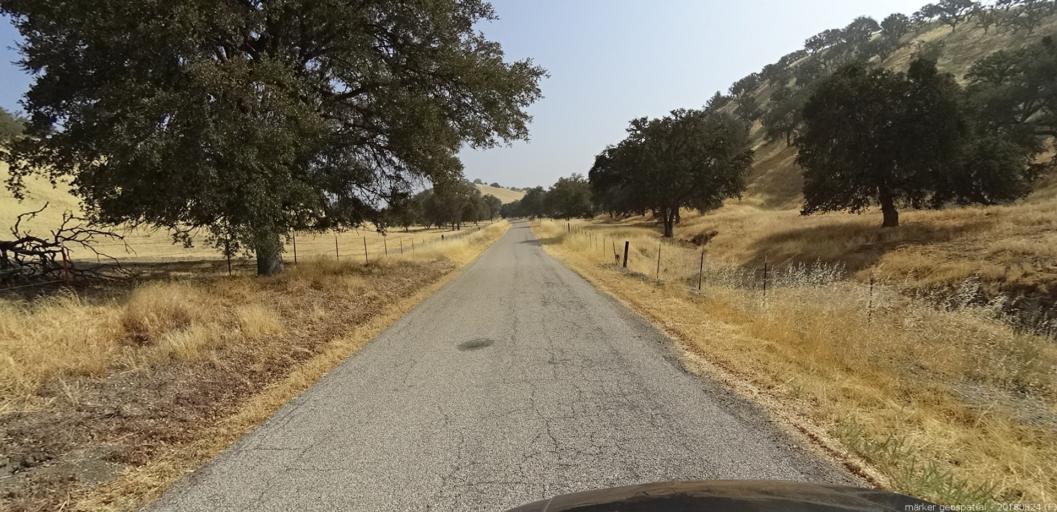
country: US
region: California
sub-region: San Luis Obispo County
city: San Miguel
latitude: 35.8812
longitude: -120.7447
